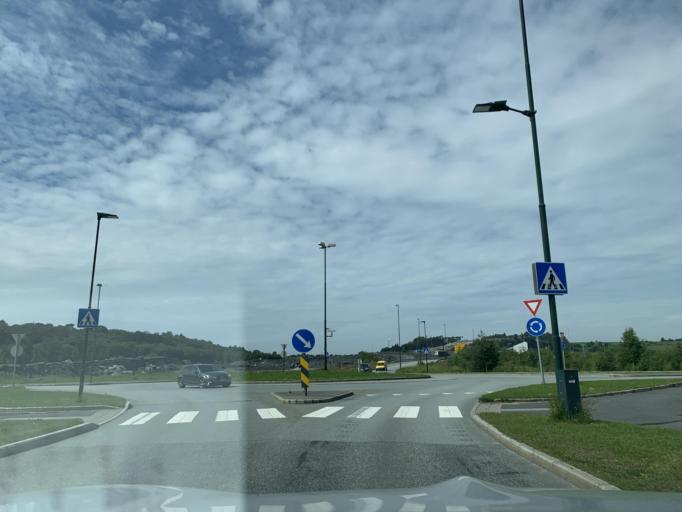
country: NO
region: Rogaland
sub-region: Sola
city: Sola
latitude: 58.8948
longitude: 5.6801
